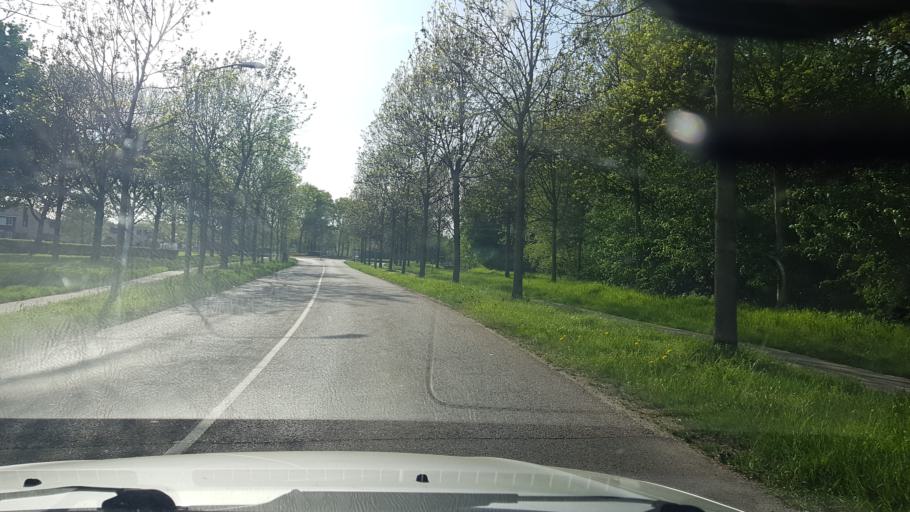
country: NL
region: Limburg
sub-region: Gemeente Sittard-Geleen
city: Sittard
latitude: 51.0078
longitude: 5.8844
